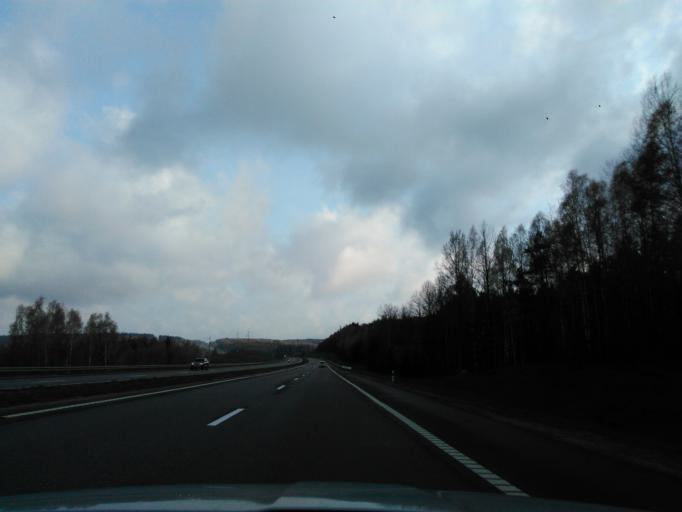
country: BY
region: Minsk
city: Lahoysk
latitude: 54.1977
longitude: 27.8166
